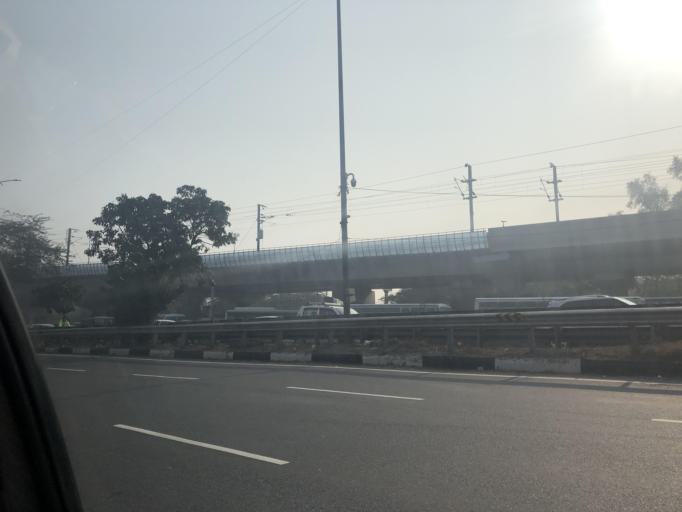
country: IN
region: NCT
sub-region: Central Delhi
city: Karol Bagh
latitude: 28.5932
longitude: 77.1635
